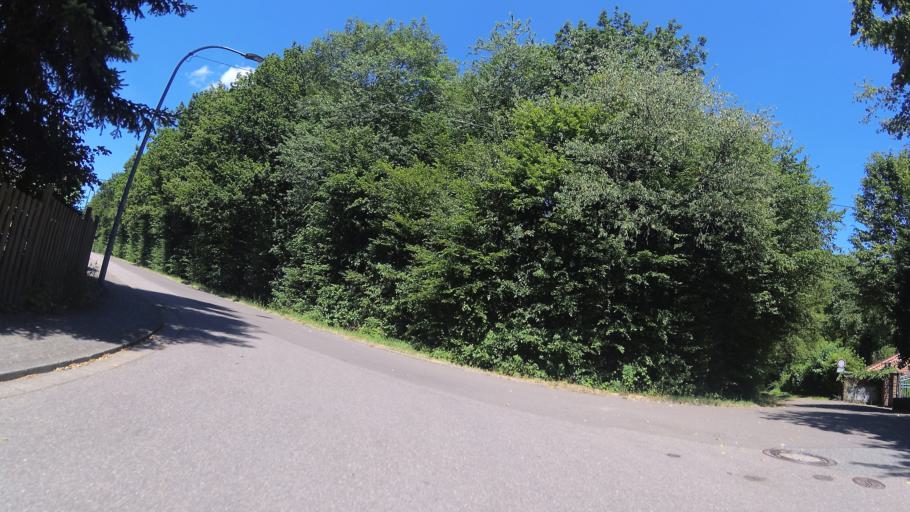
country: DE
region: Saarland
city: Neunkirchen
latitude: 49.3544
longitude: 7.1949
